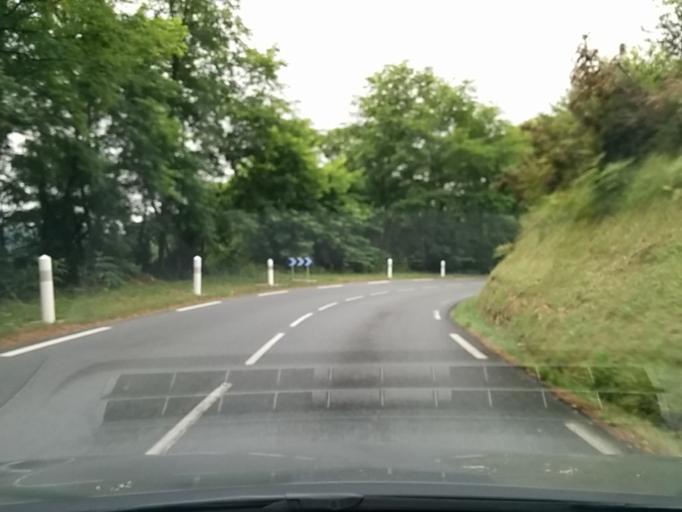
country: FR
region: Aquitaine
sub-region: Departement des Pyrenees-Atlantiques
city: Souraide
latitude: 43.3285
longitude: -1.4732
